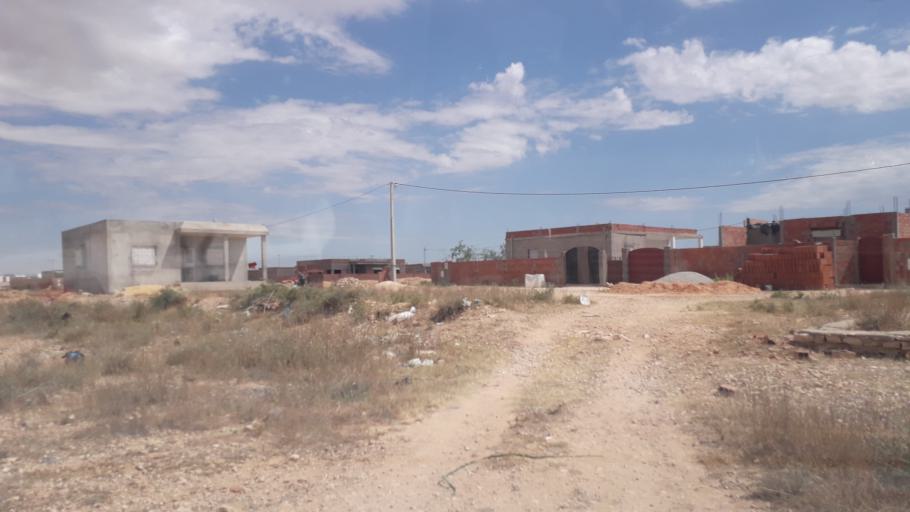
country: TN
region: Safaqis
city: Al Qarmadah
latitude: 34.8433
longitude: 10.7733
